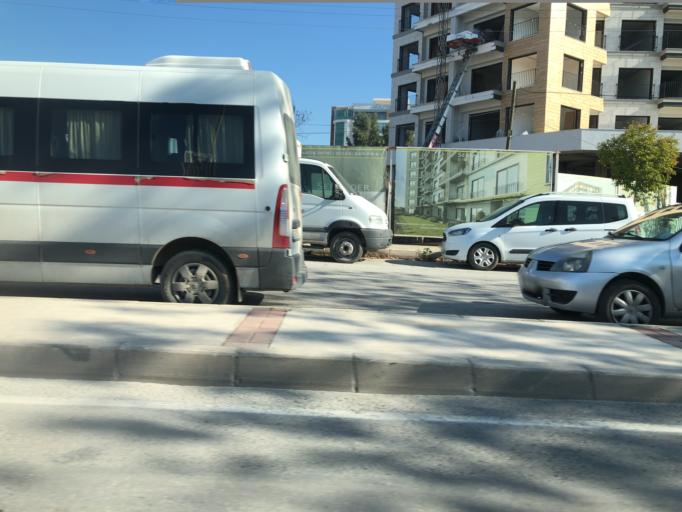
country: TR
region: Izmir
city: Izmir
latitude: 38.4593
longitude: 27.1744
